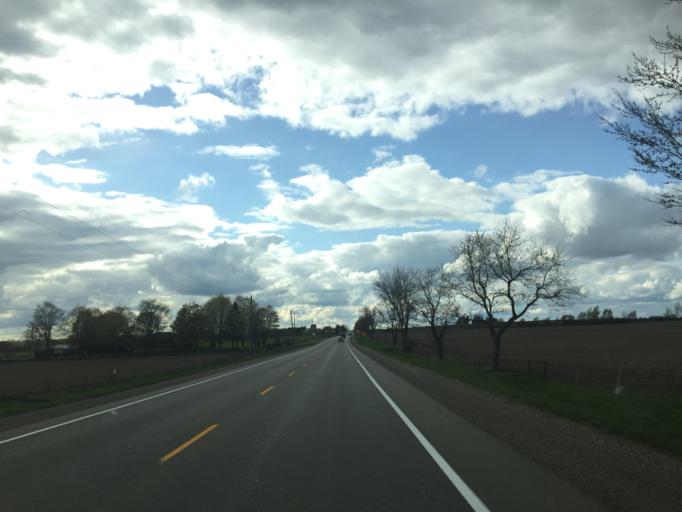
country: CA
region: Ontario
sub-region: Wellington County
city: Guelph
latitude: 43.5116
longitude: -80.3138
